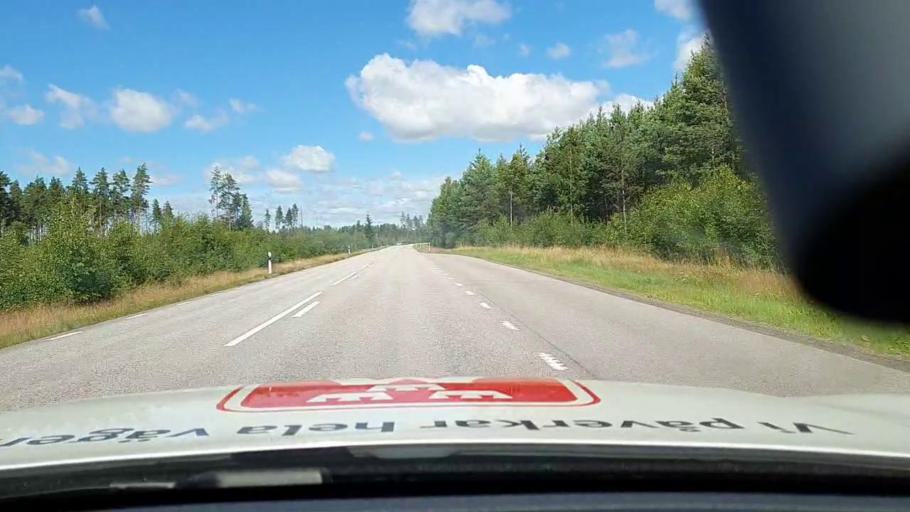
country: SE
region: Vaestra Goetaland
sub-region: Skovde Kommun
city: Stopen
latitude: 58.4405
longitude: 13.9356
